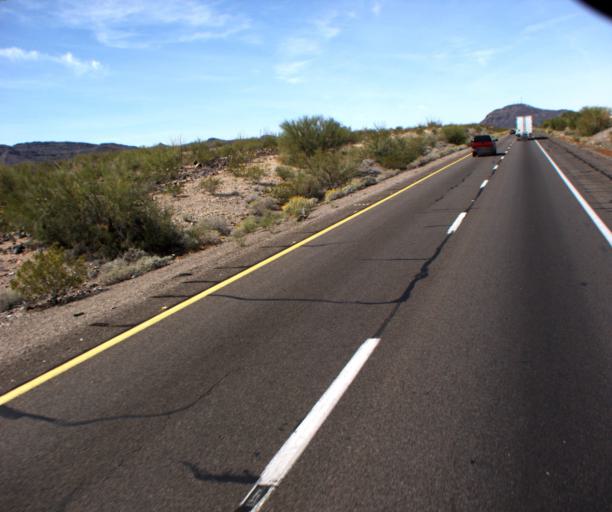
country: US
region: Arizona
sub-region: La Paz County
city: Quartzsite
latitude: 33.6606
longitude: -113.9987
